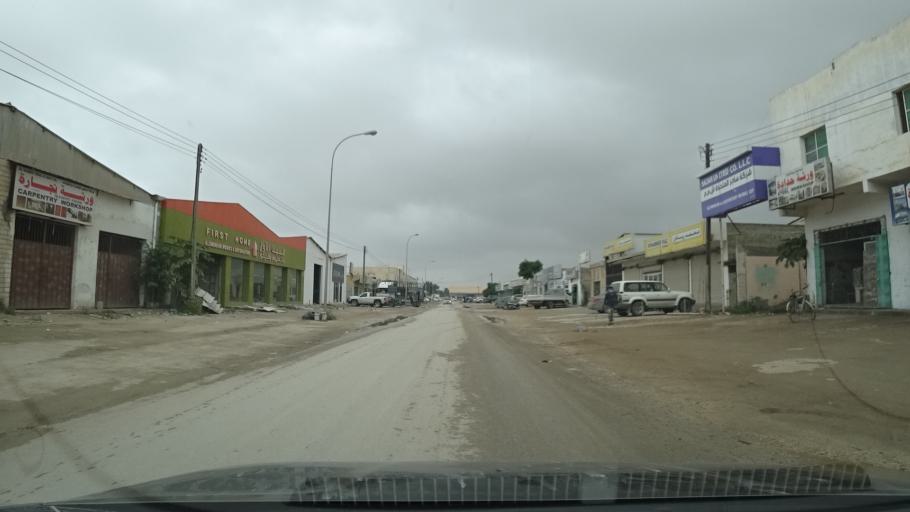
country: OM
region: Zufar
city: Salalah
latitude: 17.0152
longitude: 54.0489
